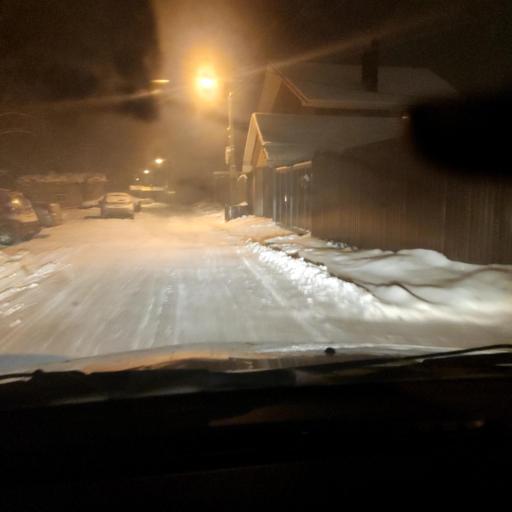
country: RU
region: Bashkortostan
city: Ufa
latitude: 54.7065
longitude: 55.9343
